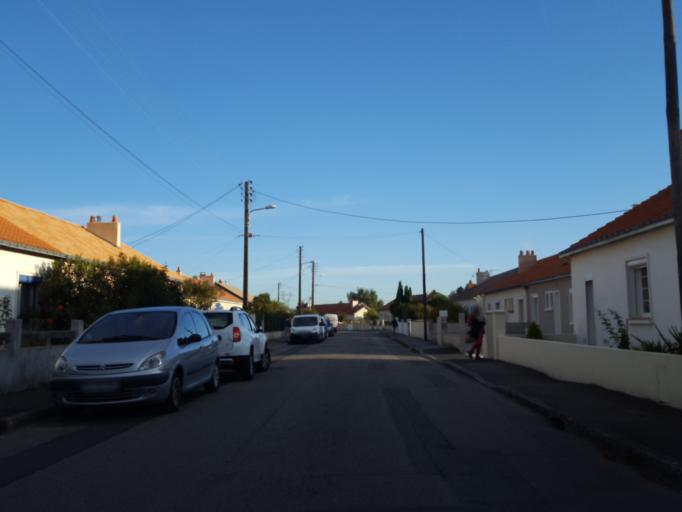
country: FR
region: Pays de la Loire
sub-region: Departement de la Loire-Atlantique
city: Saint-Sebastien-sur-Loire
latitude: 47.1970
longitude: -1.4877
